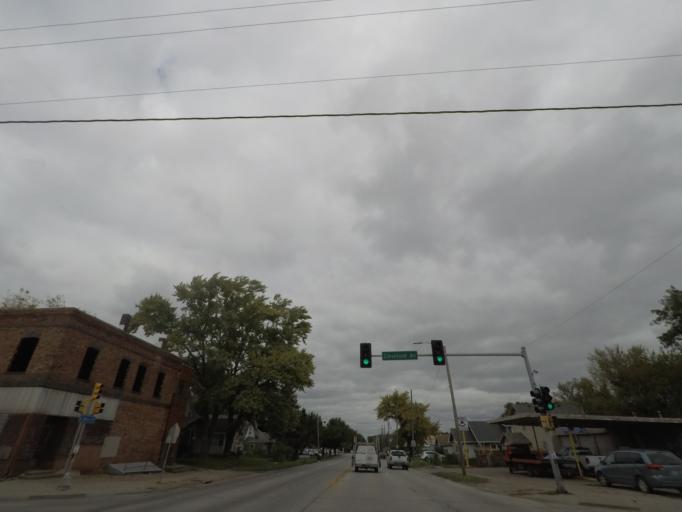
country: US
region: Iowa
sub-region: Polk County
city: Des Moines
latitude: 41.6050
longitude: -93.6005
